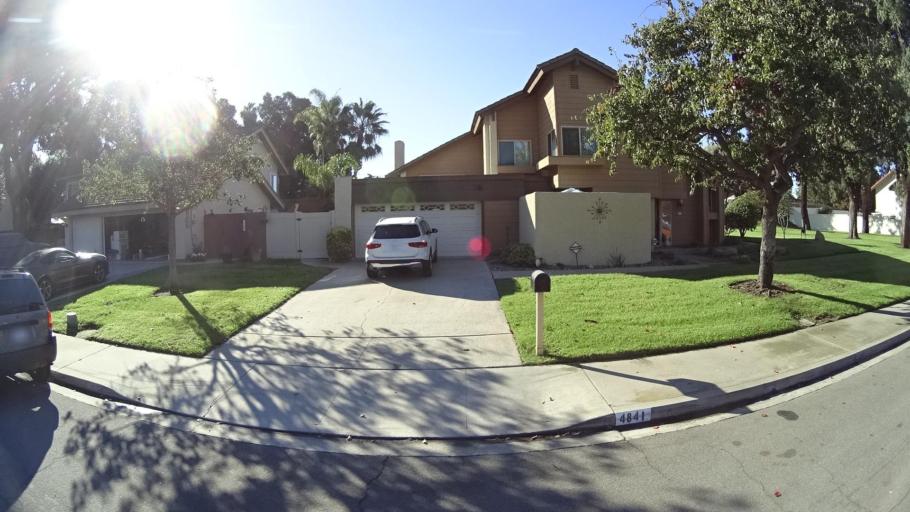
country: US
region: California
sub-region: San Diego County
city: Bonita
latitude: 32.6748
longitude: -117.0272
